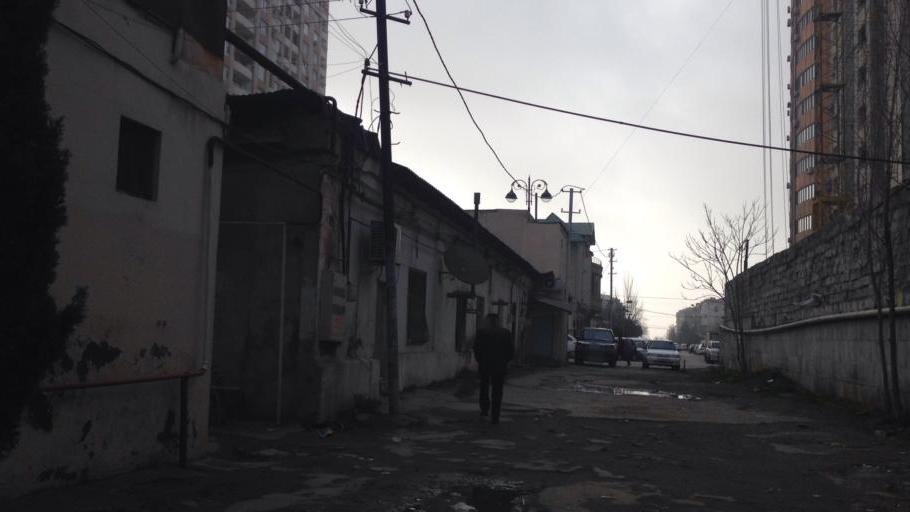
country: AZ
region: Baki
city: Baku
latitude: 40.3816
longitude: 49.8677
